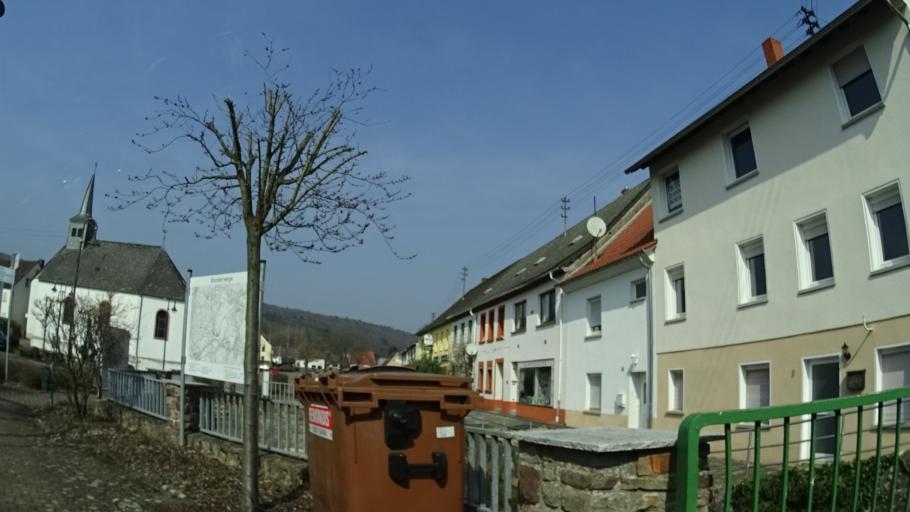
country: DE
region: Rheinland-Pfalz
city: Hoppstadten-Weiersbach
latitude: 49.6185
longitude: 7.1974
